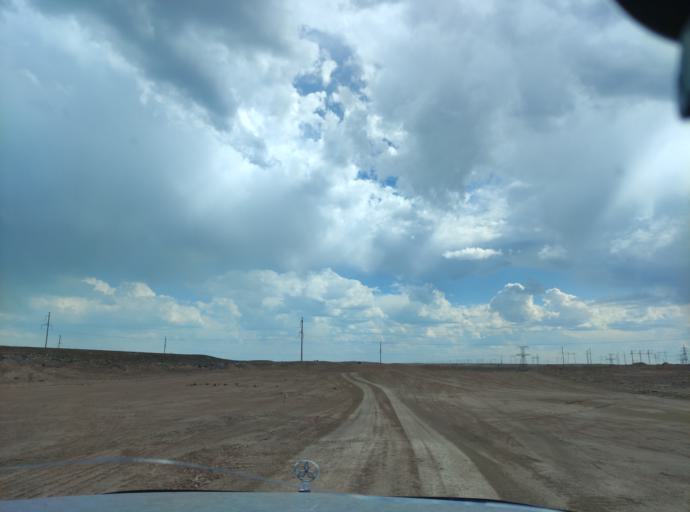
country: KZ
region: Qaraghandy
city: Saryshaghan
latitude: 46.1248
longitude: 73.5962
